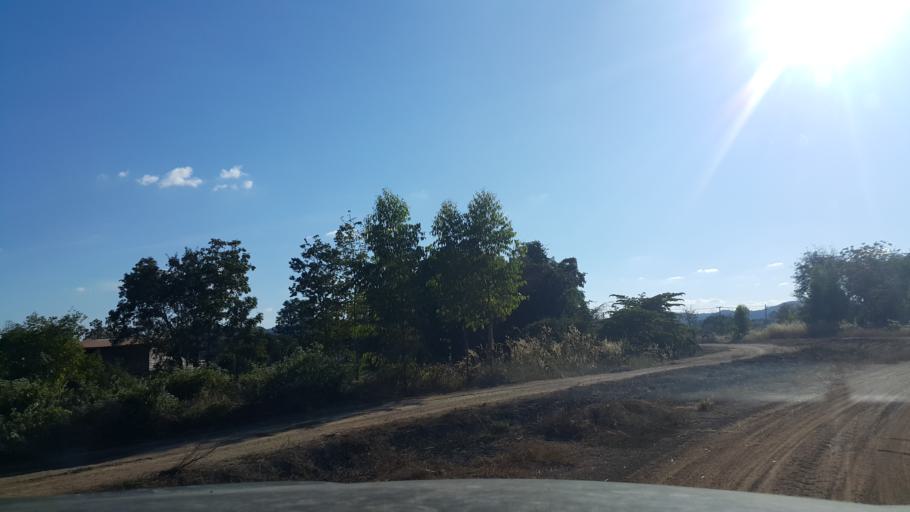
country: TH
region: Sukhothai
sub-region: Amphoe Si Satchanalai
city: Si Satchanalai
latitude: 17.4654
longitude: 99.6612
